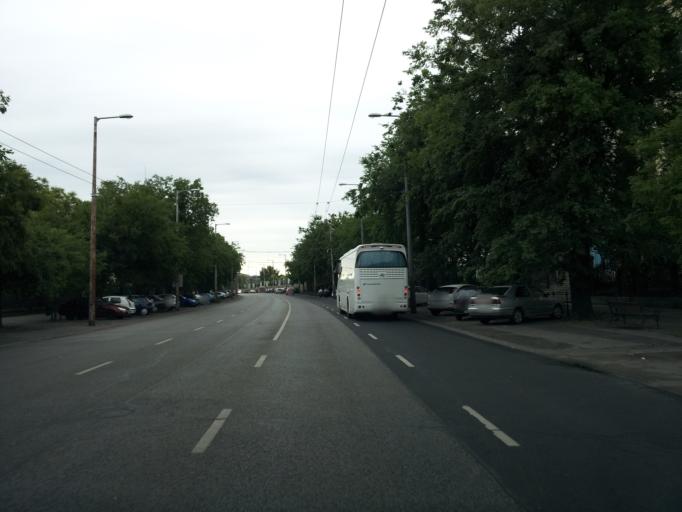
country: HU
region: Budapest
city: Budapest XIV. keruelet
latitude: 47.5062
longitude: 19.0974
